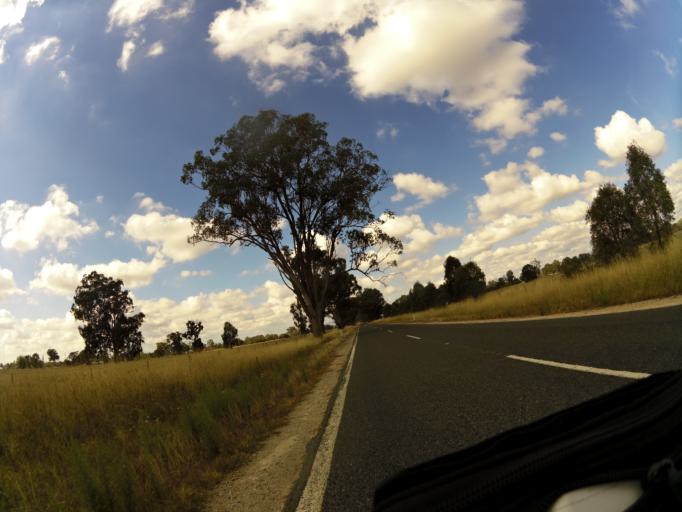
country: AU
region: Victoria
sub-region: Benalla
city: Benalla
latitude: -36.6005
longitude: 146.0114
